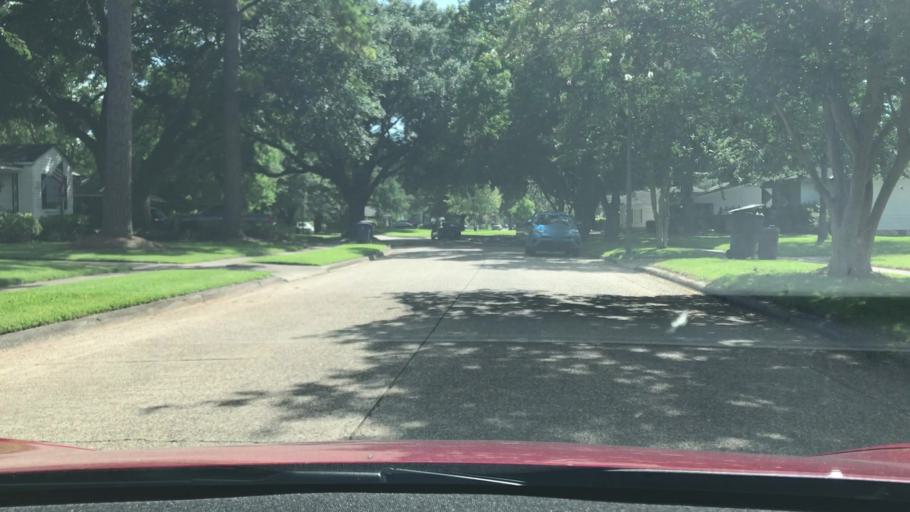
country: US
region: Louisiana
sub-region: Bossier Parish
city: Bossier City
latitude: 32.4630
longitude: -93.7123
